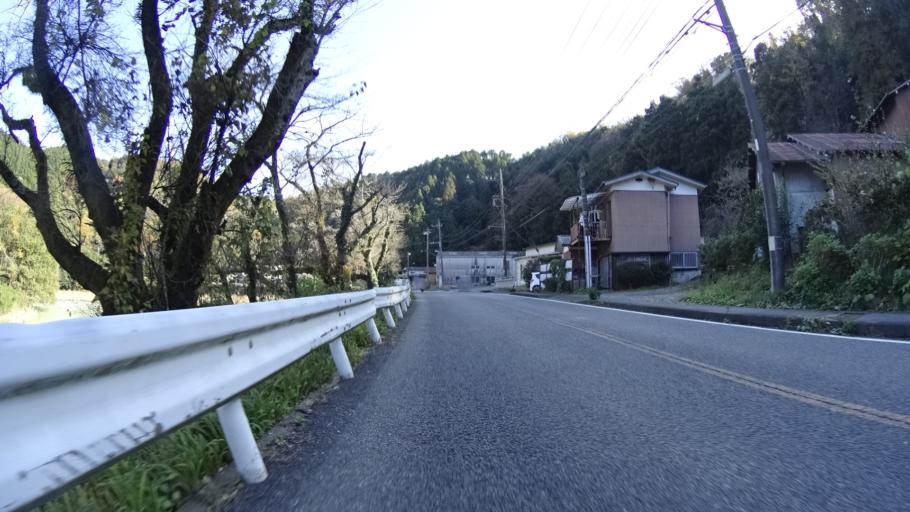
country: JP
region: Kanagawa
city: Zama
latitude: 35.5356
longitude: 139.2798
